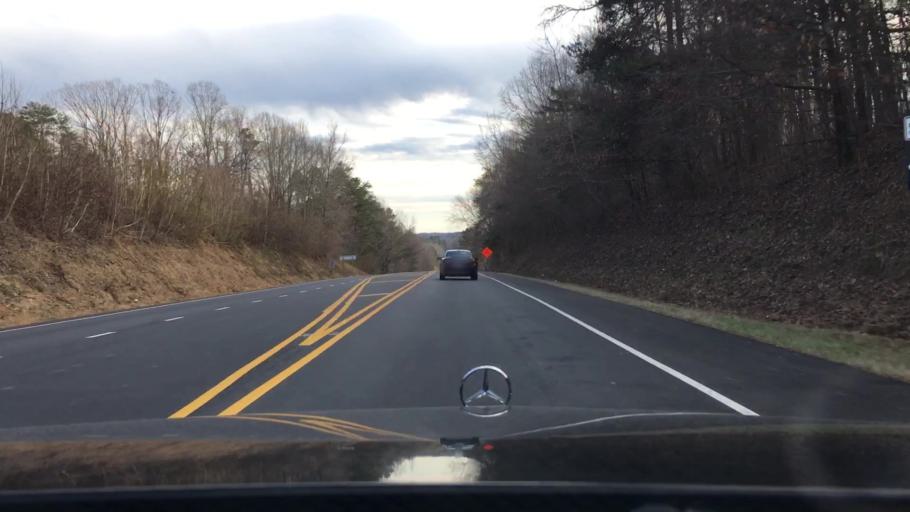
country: US
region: North Carolina
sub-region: Caswell County
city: Yanceyville
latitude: 36.4878
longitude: -79.3827
